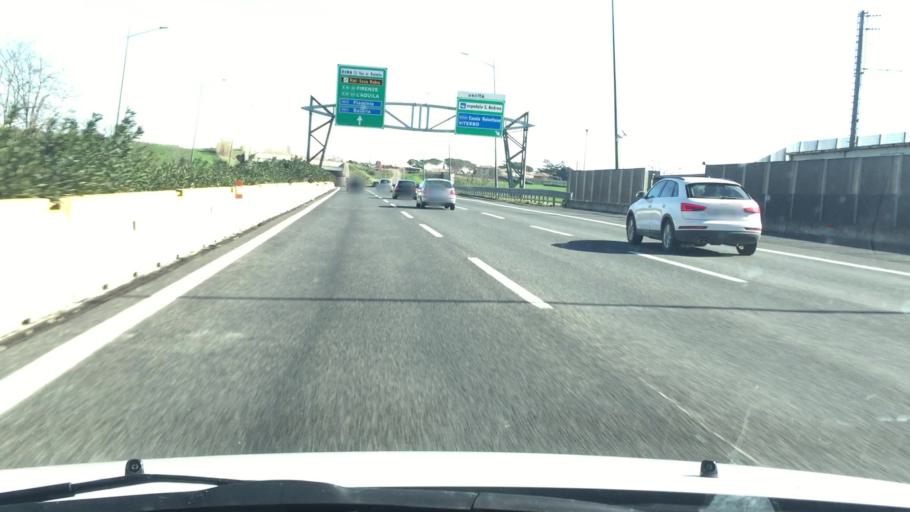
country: VA
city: Vatican City
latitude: 41.9812
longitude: 12.4548
